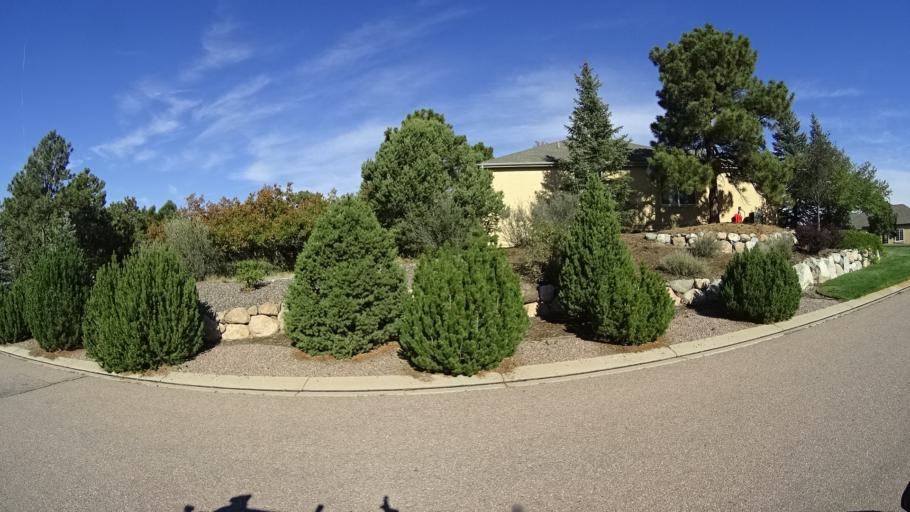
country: US
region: Colorado
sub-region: El Paso County
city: Colorado Springs
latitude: 38.9110
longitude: -104.7946
